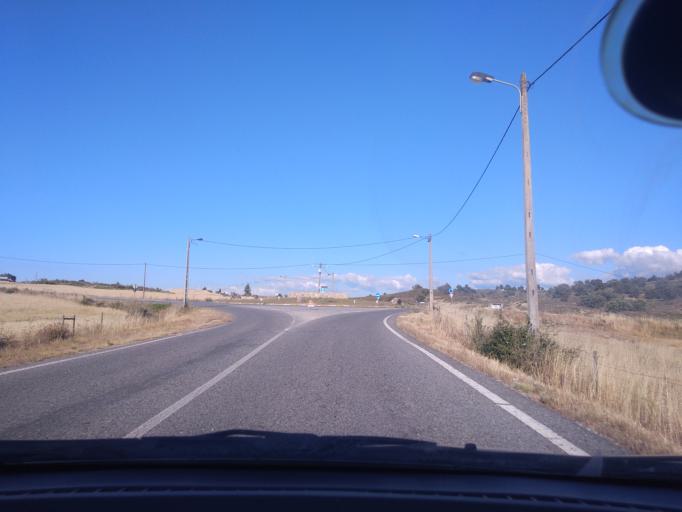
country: PT
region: Castelo Branco
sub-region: Covilha
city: Teixoso
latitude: 40.2498
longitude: -7.3922
